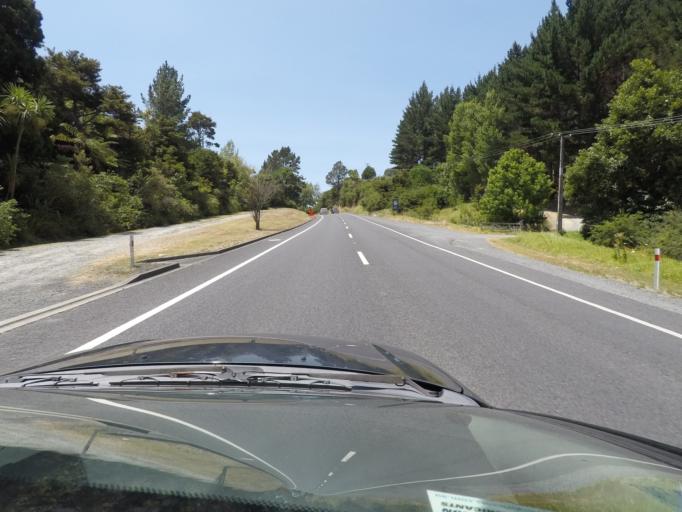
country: NZ
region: Auckland
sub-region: Auckland
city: Warkworth
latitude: -36.3489
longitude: 174.7232
